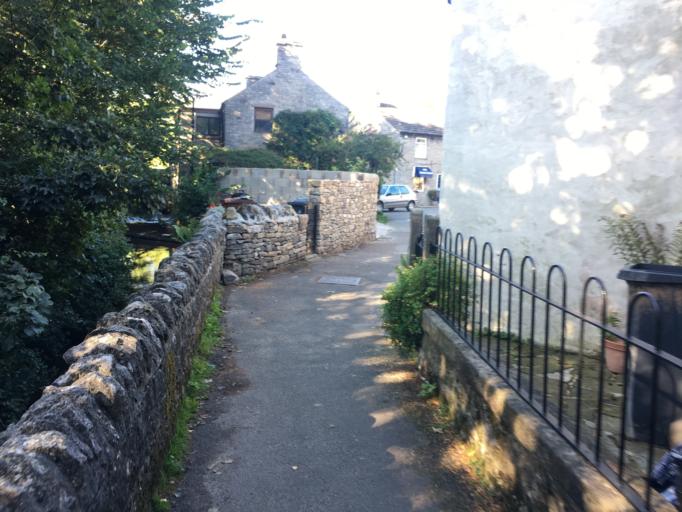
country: GB
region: England
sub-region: Derbyshire
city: Hope Valley
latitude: 53.3429
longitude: -1.7778
